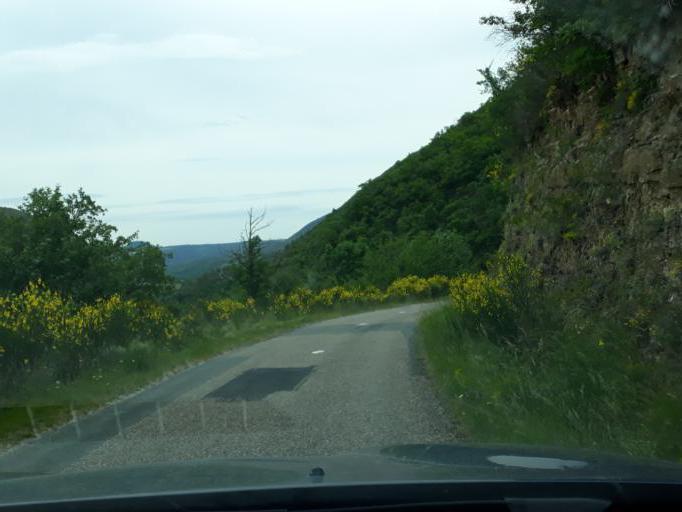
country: FR
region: Languedoc-Roussillon
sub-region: Departement de l'Herault
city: Lodeve
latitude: 43.7959
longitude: 3.2711
